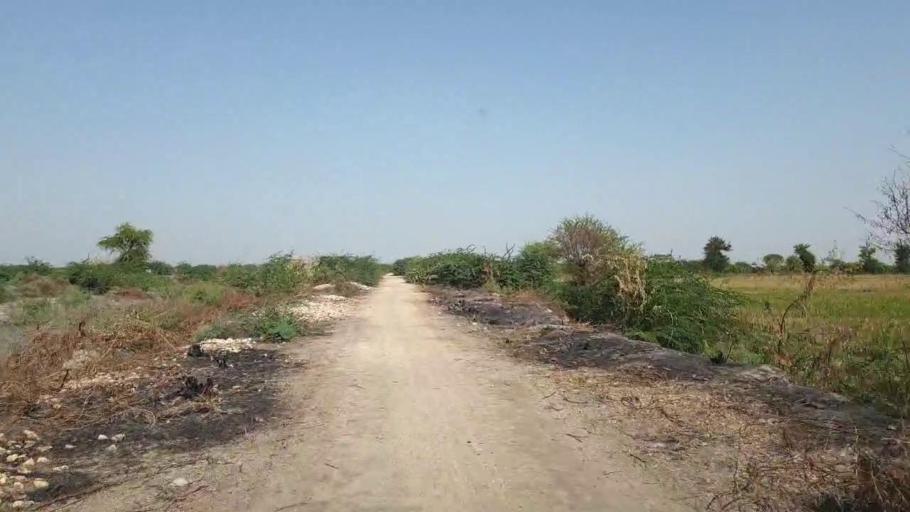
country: PK
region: Sindh
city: Tando Bago
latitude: 24.7187
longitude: 69.0729
